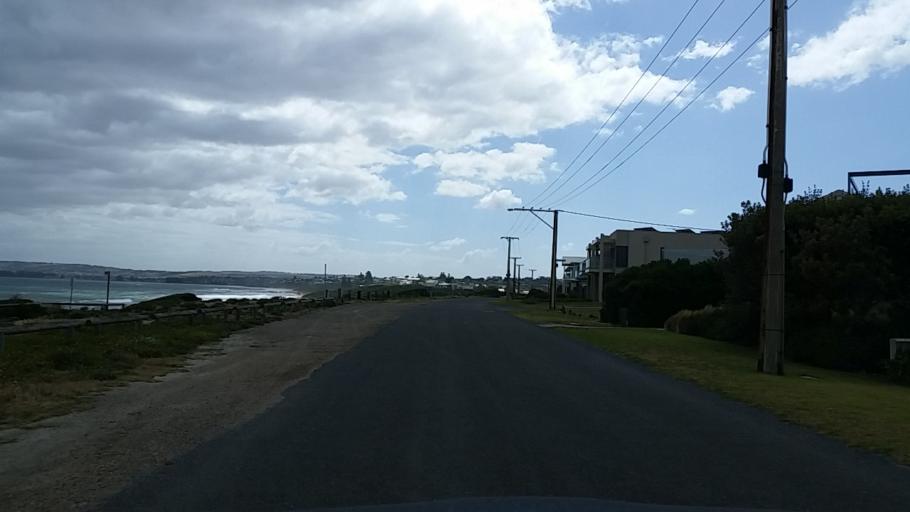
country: AU
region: South Australia
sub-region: Alexandrina
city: Port Elliot
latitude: -35.5355
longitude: 138.6678
